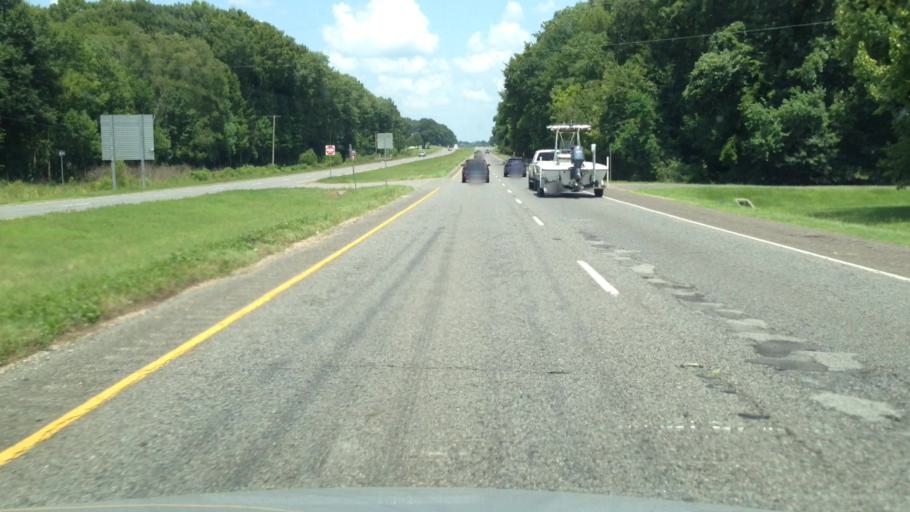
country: US
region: Louisiana
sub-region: Saint Landry Parish
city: Opelousas
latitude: 30.5379
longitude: -92.0514
